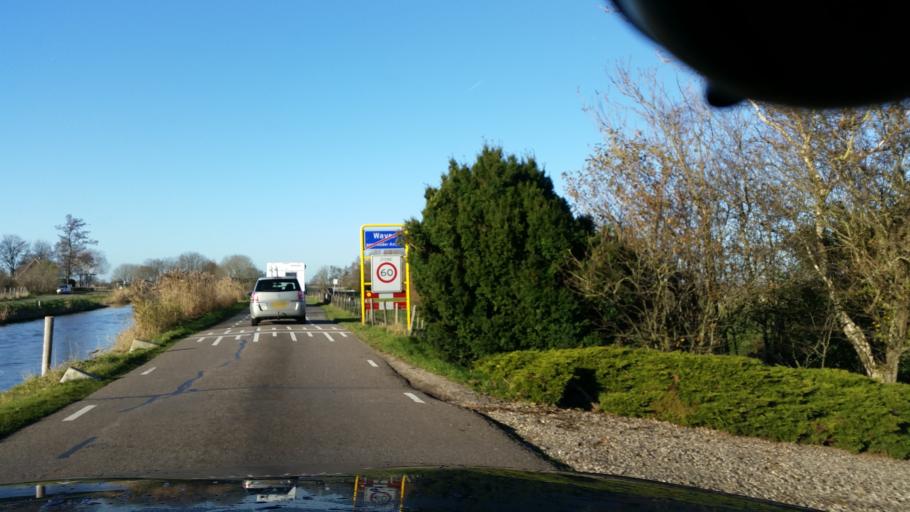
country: NL
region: North Holland
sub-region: Gemeente Ouder-Amstel
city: Ouderkerk aan de Amstel
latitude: 52.2531
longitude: 4.9070
